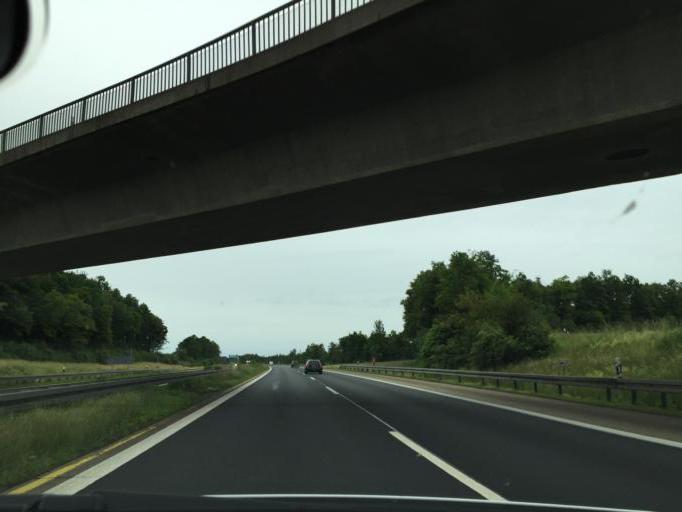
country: DE
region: Bavaria
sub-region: Regierungsbezirk Unterfranken
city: Riedenberg
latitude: 50.2964
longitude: 9.8493
